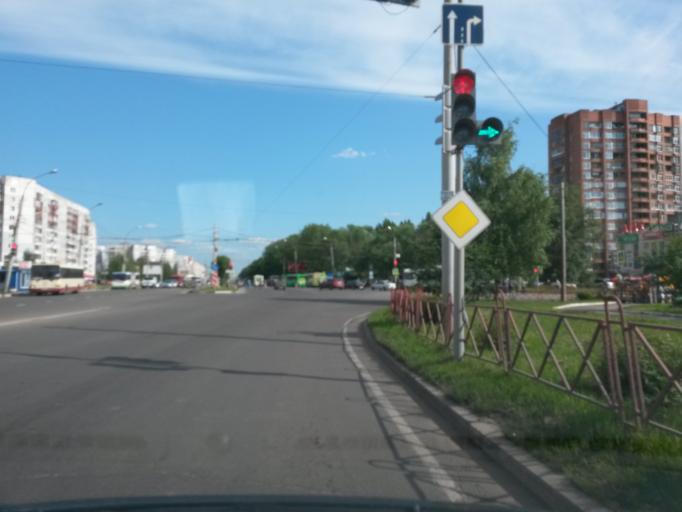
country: RU
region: Jaroslavl
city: Yaroslavl
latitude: 57.6962
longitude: 39.7667
